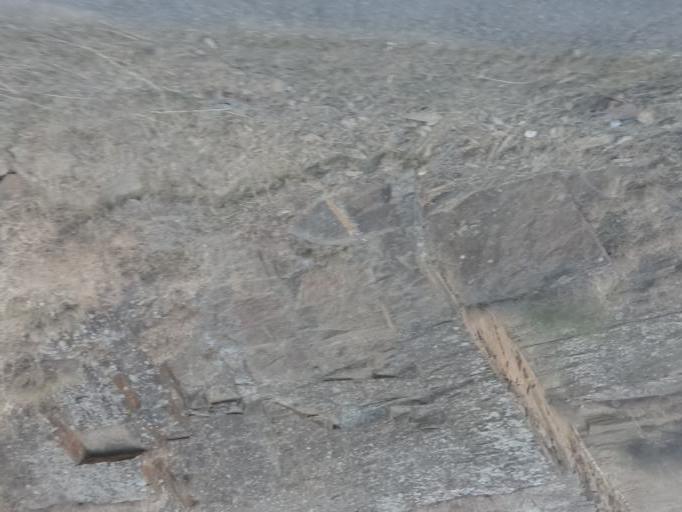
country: PT
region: Viseu
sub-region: Armamar
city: Armamar
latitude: 41.1591
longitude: -7.6802
